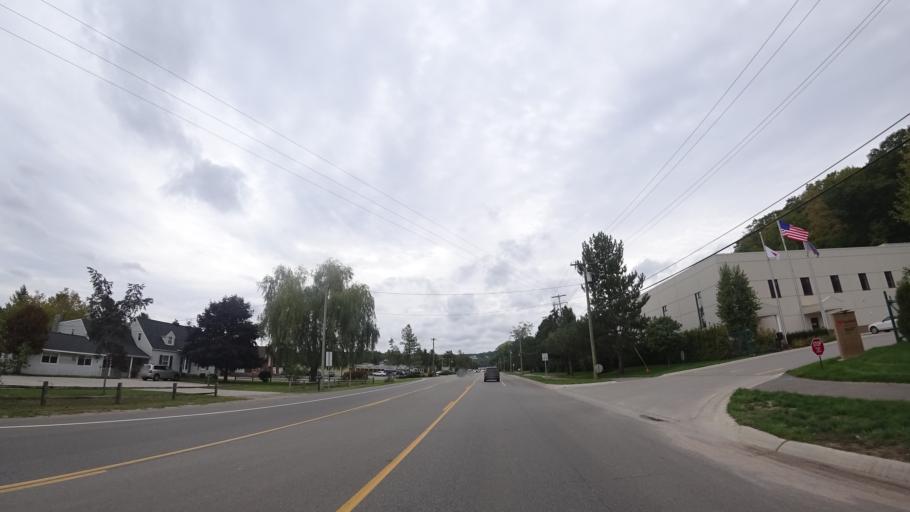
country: US
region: Michigan
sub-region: Emmet County
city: Petoskey
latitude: 45.4050
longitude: -84.9021
